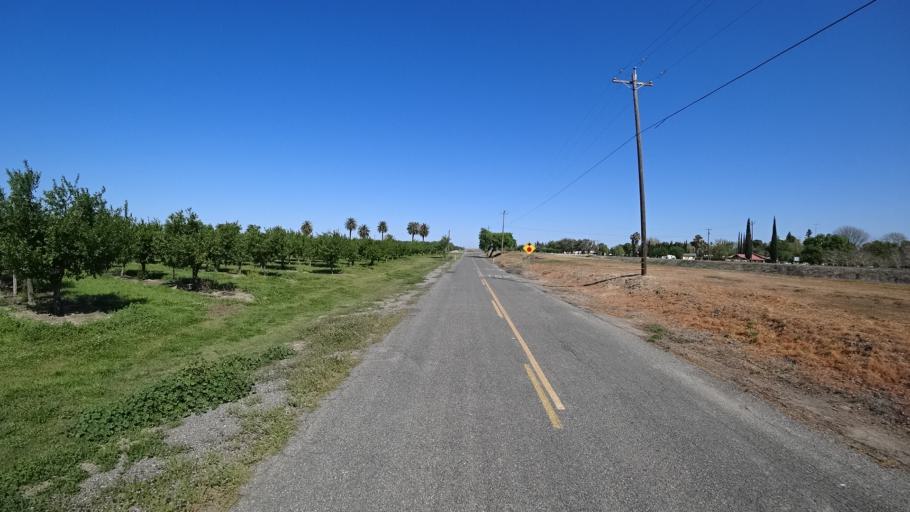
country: US
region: California
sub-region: Glenn County
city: Hamilton City
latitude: 39.7358
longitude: -122.0163
